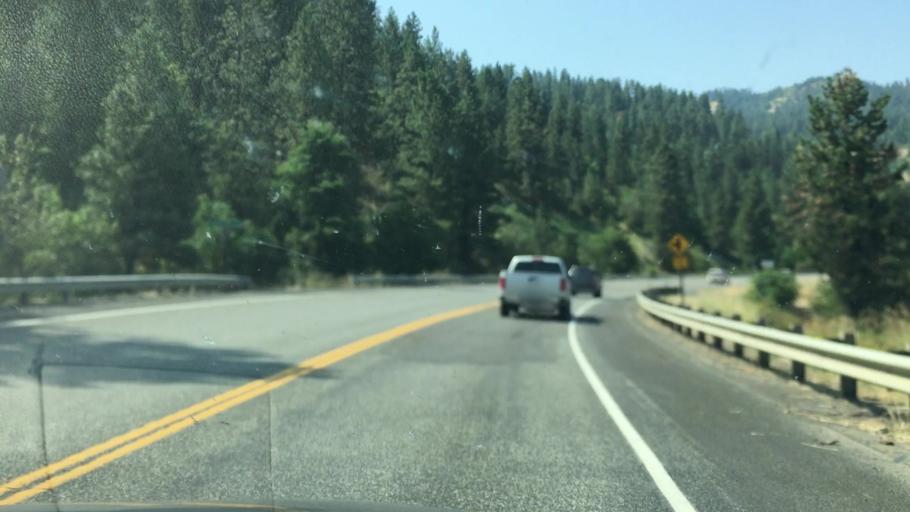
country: US
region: Idaho
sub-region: Nez Perce County
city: Lapwai
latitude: 46.5072
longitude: -116.5641
